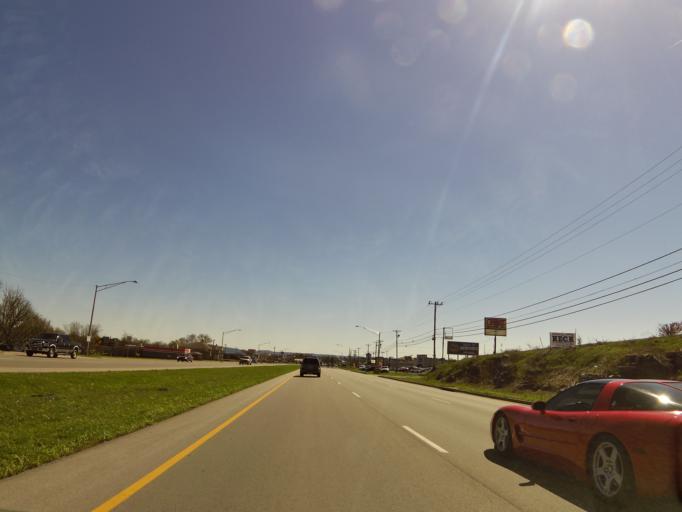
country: US
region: Kentucky
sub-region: Pulaski County
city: Somerset
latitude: 37.0713
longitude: -84.6188
